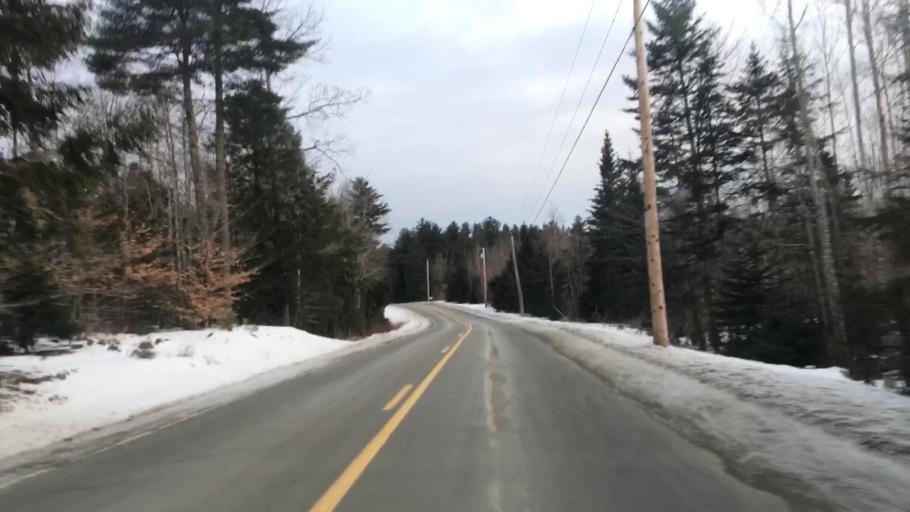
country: US
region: Maine
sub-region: Hancock County
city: Franklin
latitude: 44.7618
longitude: -68.3249
